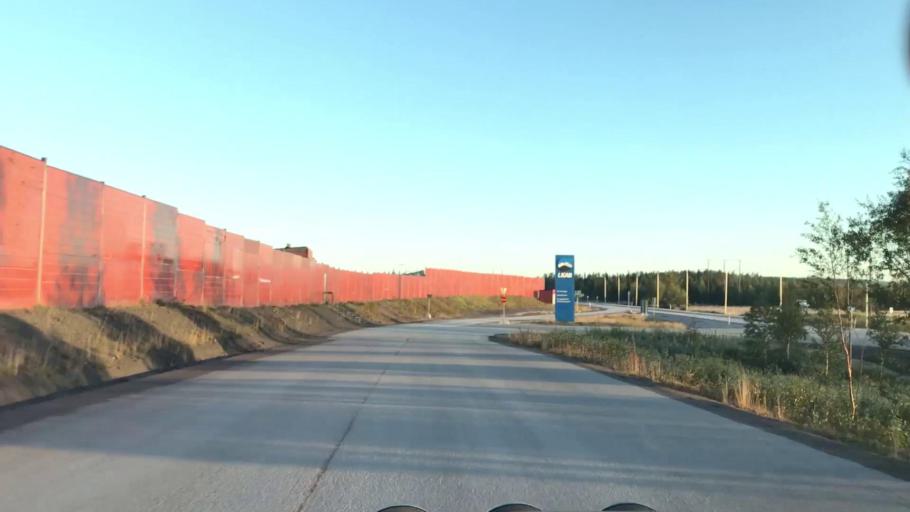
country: SE
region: Norrbotten
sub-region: Gallivare Kommun
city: Malmberget
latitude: 67.6516
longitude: 21.0167
